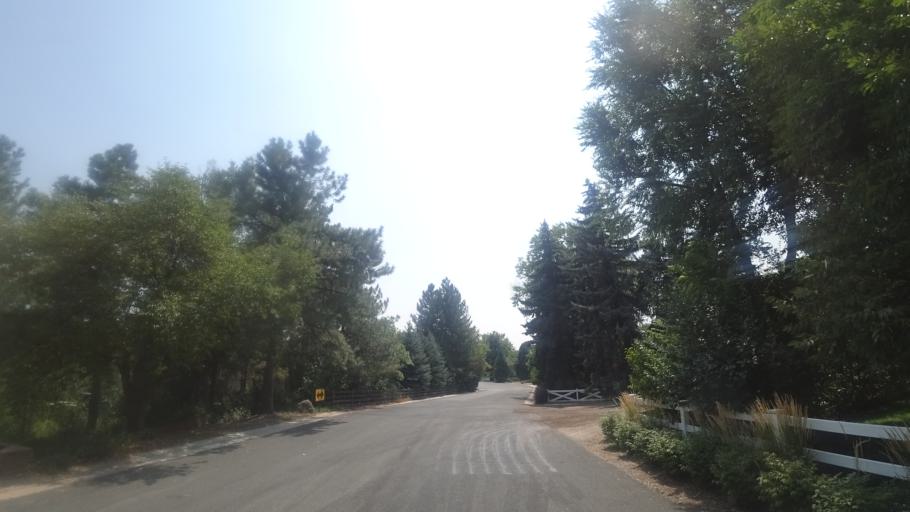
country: US
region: Colorado
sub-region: Arapahoe County
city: Cherry Hills Village
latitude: 39.6262
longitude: -104.9675
